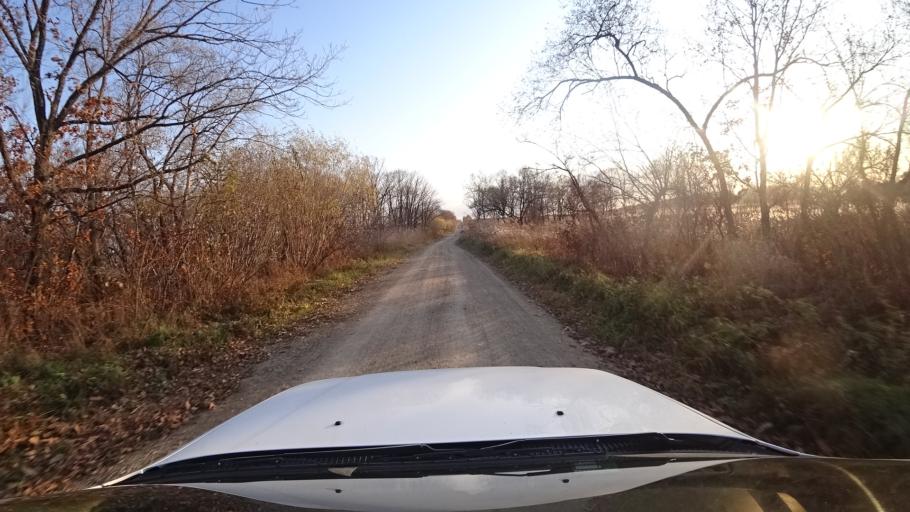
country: RU
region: Primorskiy
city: Lazo
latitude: 45.8159
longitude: 133.6111
